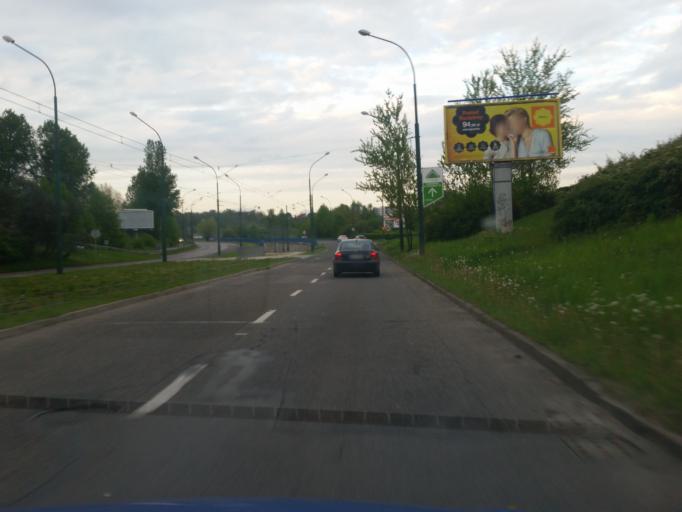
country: PL
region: Silesian Voivodeship
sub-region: Powiat bedzinski
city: Bedzin
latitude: 50.2942
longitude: 19.1682
